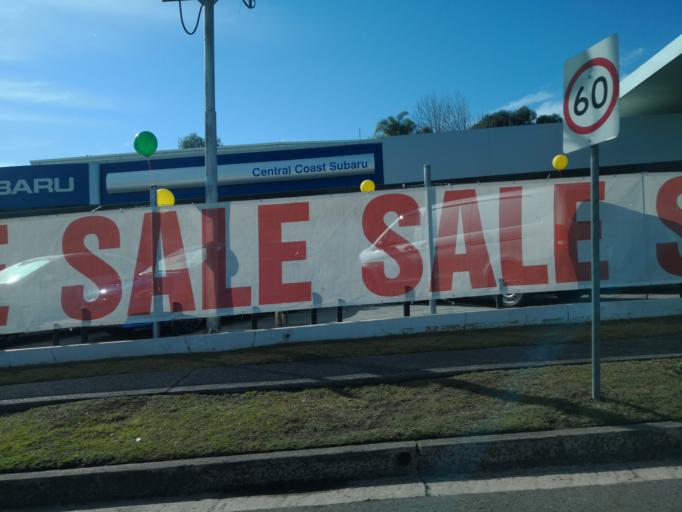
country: AU
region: New South Wales
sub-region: Gosford Shire
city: Gosford
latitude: -33.4166
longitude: 151.3440
